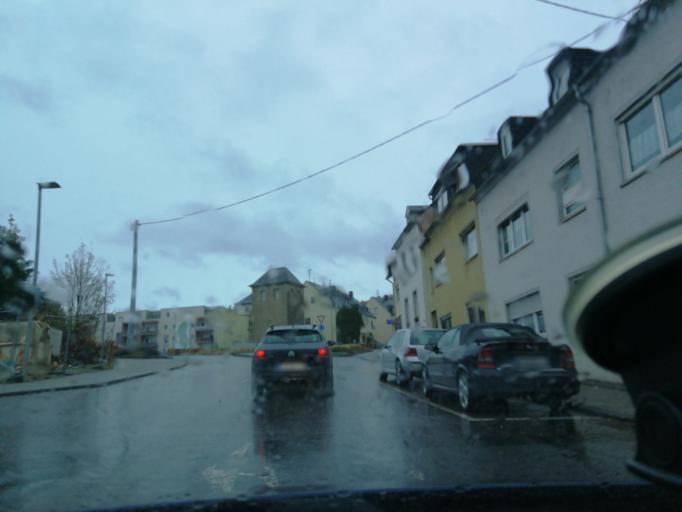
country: DE
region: Rheinland-Pfalz
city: Trier
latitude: 49.7263
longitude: 6.6304
